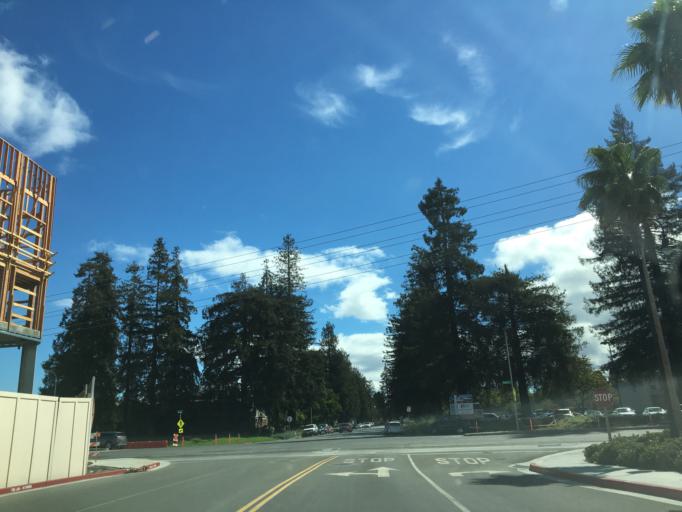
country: US
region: California
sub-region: Santa Clara County
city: Santa Clara
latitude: 37.3806
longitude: -121.9746
